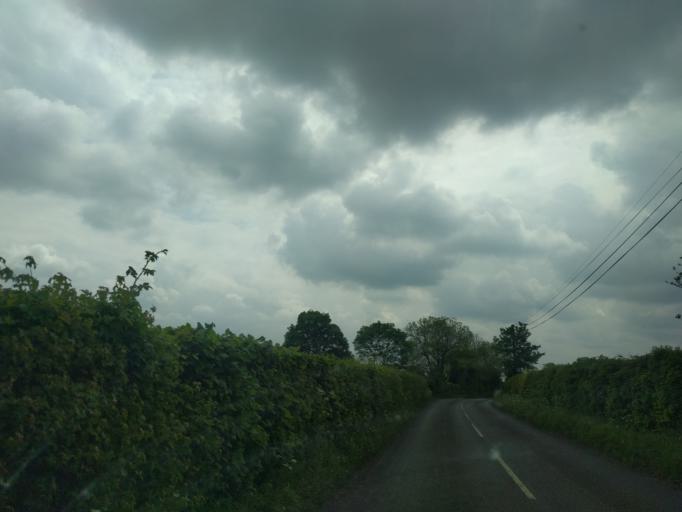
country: GB
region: England
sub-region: Somerset
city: Langport
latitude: 51.0712
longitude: -2.8214
